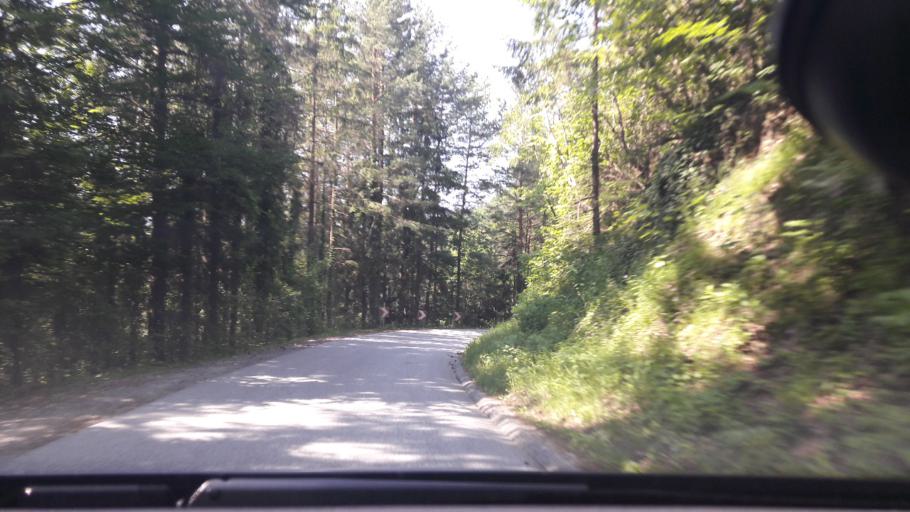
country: AT
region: Styria
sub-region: Politischer Bezirk Graz-Umgebung
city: Stiwoll
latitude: 47.1095
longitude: 15.1929
